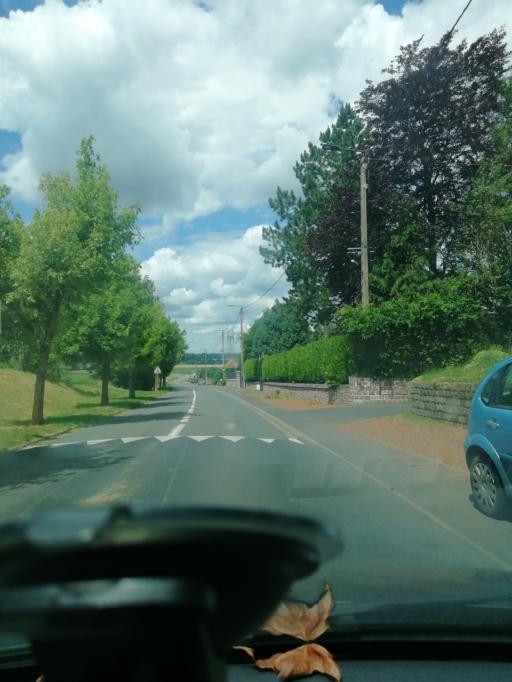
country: FR
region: Nord-Pas-de-Calais
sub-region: Departement du Nord
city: Monchecourt
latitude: 50.3048
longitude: 3.1776
